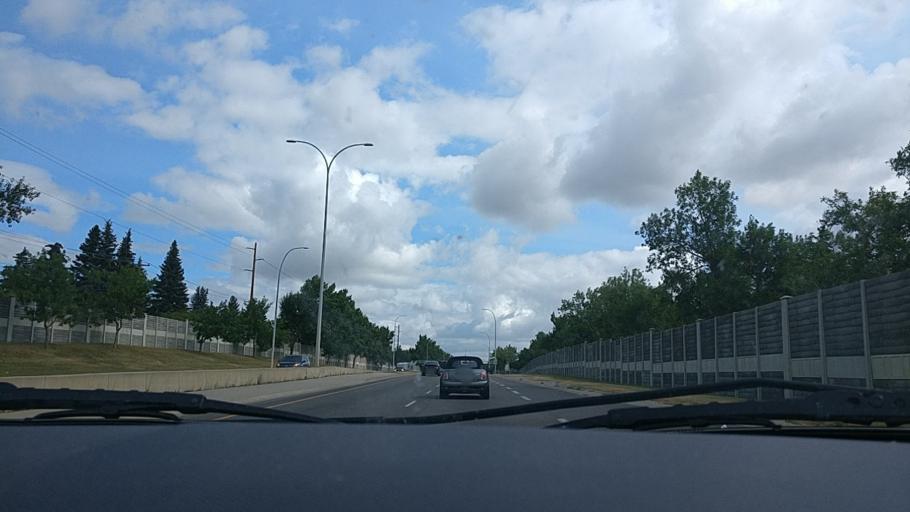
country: CA
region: Alberta
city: Calgary
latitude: 51.0911
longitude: -114.0895
